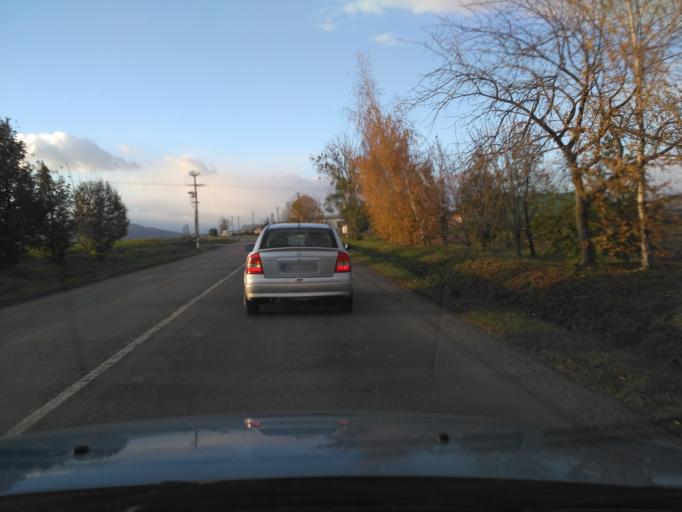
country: SK
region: Kosicky
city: Secovce
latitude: 48.6545
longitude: 21.6734
